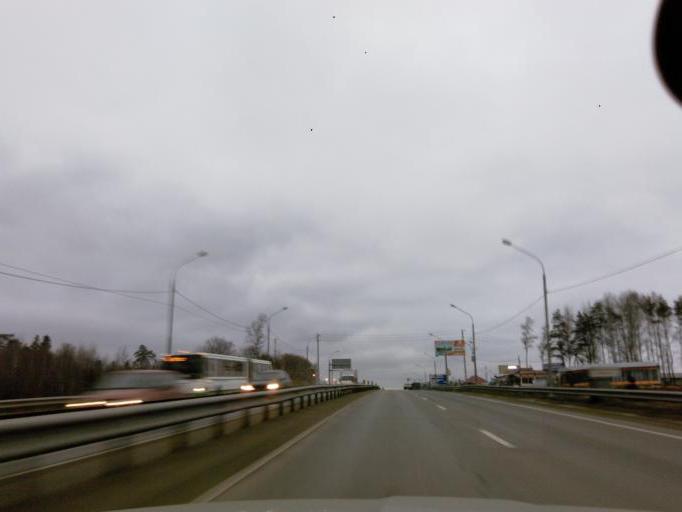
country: RU
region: Moskovskaya
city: Radumlya
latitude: 56.0672
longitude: 37.1369
